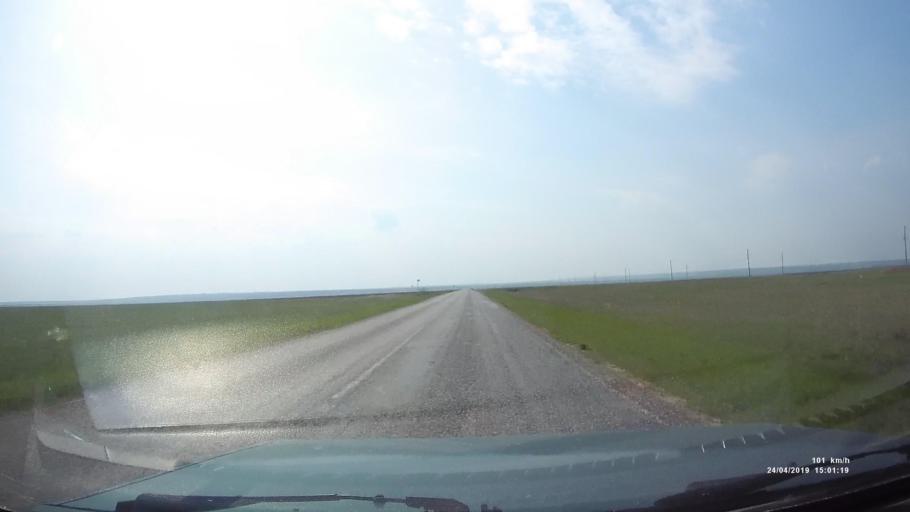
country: RU
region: Rostov
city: Remontnoye
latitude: 46.5658
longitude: 43.5364
